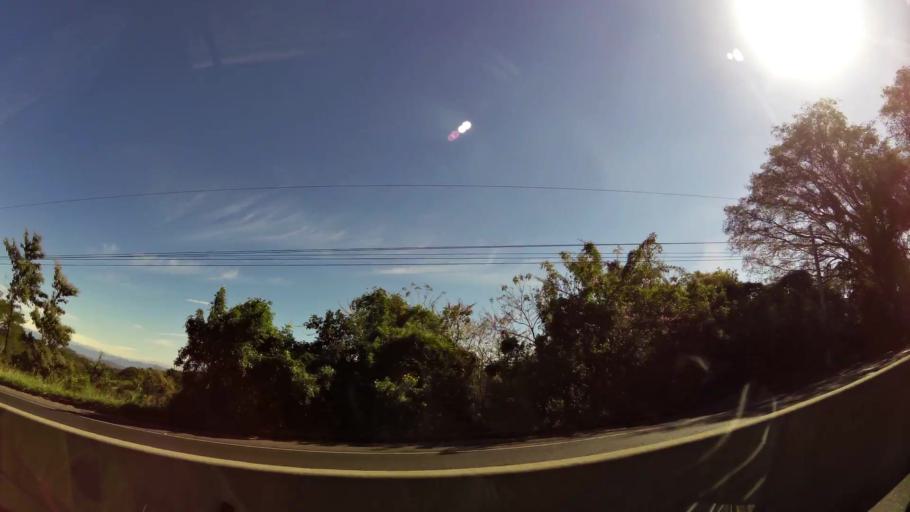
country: SV
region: Santa Ana
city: Coatepeque
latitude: 13.9222
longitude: -89.5189
